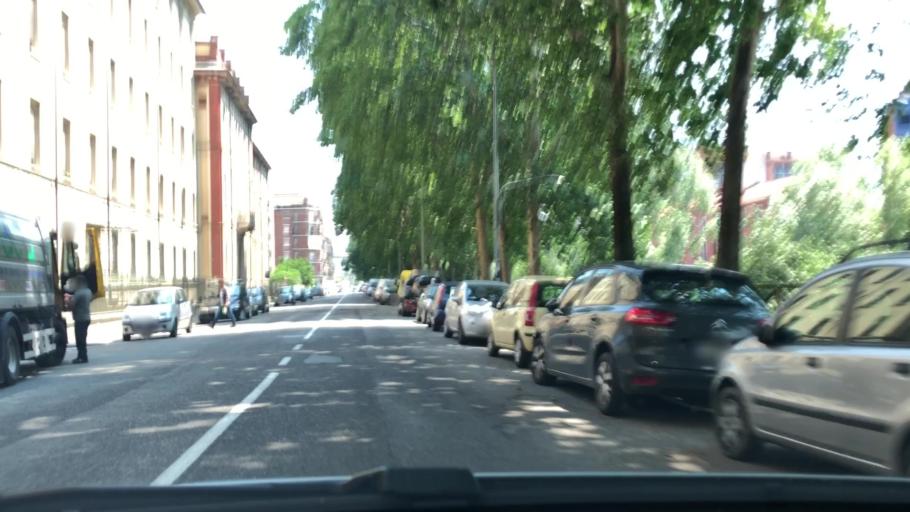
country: IT
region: Piedmont
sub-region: Provincia di Torino
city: Turin
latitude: 45.0874
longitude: 7.6774
